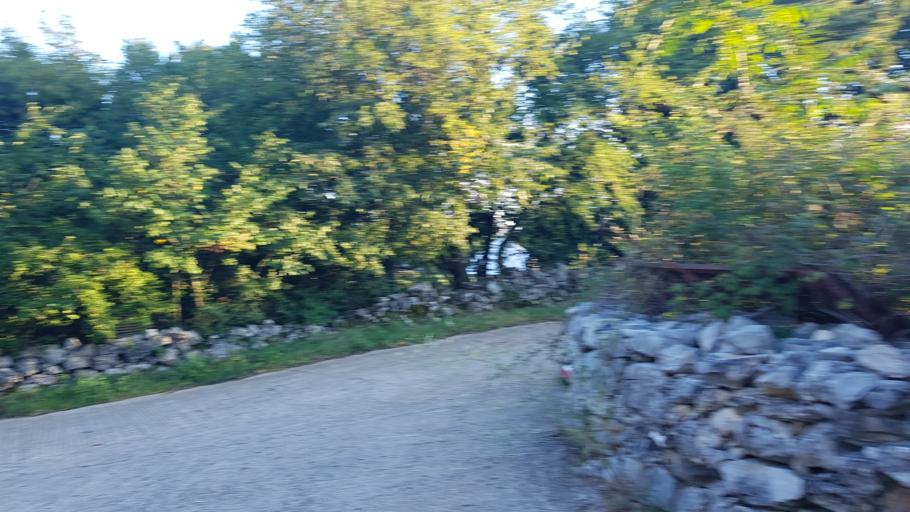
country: IT
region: Friuli Venezia Giulia
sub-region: Provincia di Trieste
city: Sistiana-Visogliano
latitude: 45.7897
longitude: 13.6375
